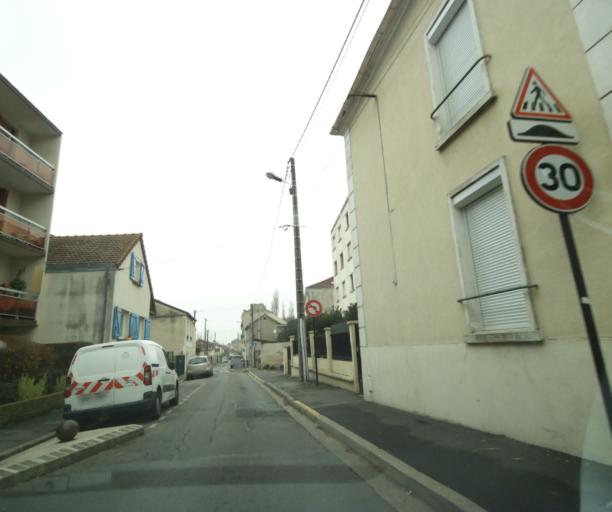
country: FR
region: Ile-de-France
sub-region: Departement de Seine-Saint-Denis
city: Livry-Gargan
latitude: 48.9231
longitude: 2.5427
